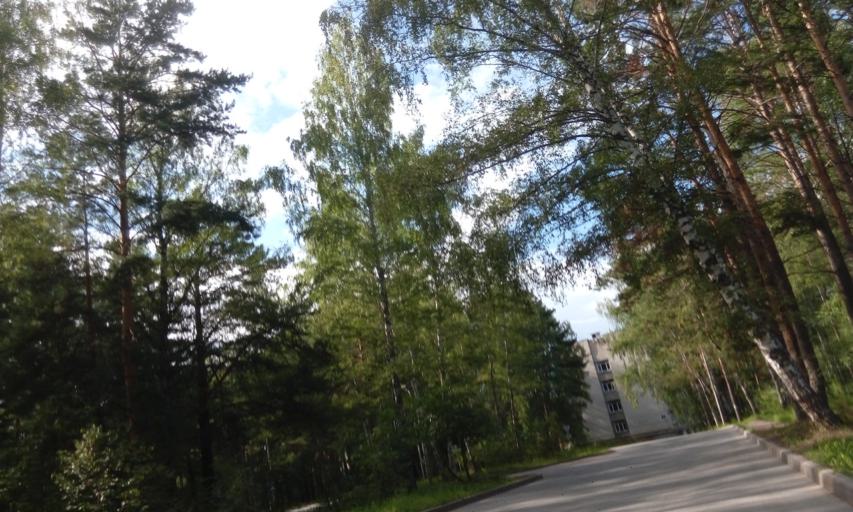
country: RU
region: Novosibirsk
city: Akademgorodok
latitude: 54.8429
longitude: 83.0971
